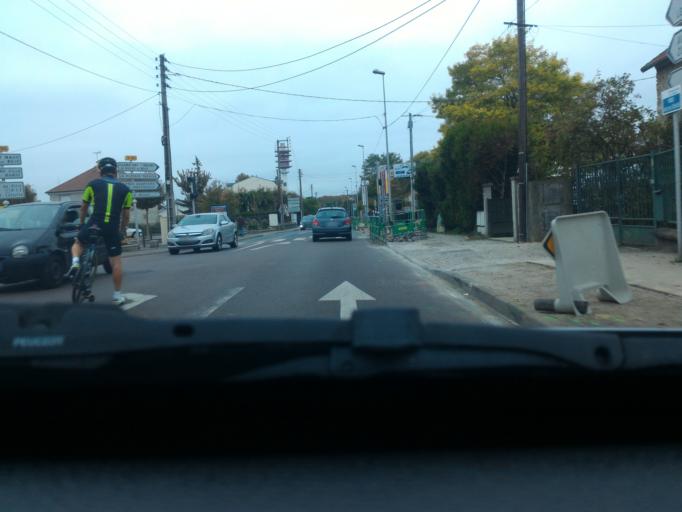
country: FR
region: Ile-de-France
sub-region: Departement du Val-de-Marne
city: Chennevieres-sur-Marne
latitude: 48.7962
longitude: 2.5336
